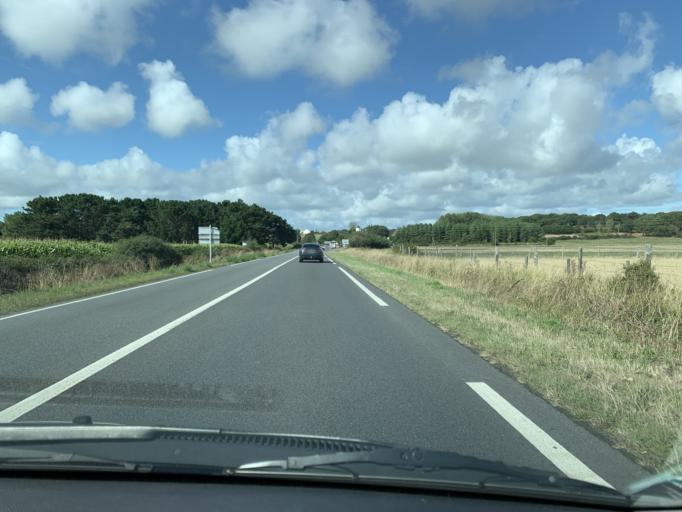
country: FR
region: Pays de la Loire
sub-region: Departement de la Loire-Atlantique
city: Guerande
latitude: 47.3117
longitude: -2.4294
